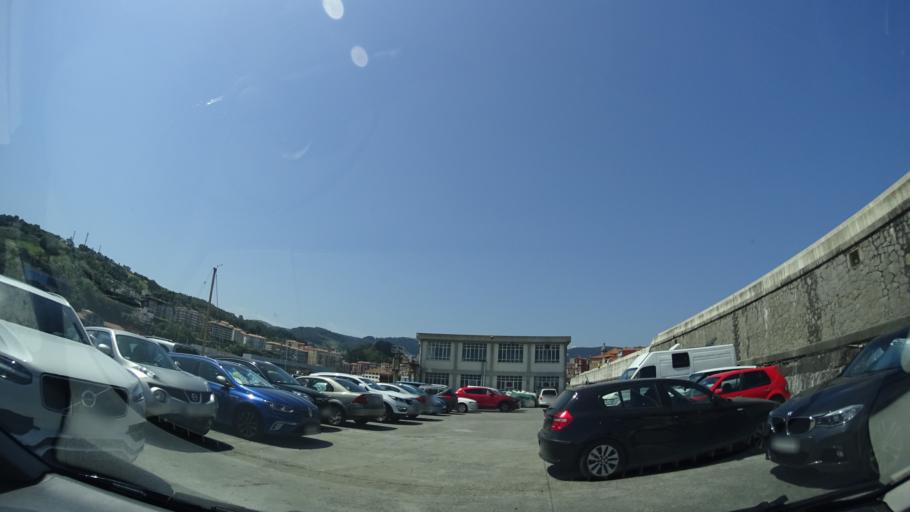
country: ES
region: Basque Country
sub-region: Bizkaia
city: Bermeo
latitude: 43.4204
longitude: -2.7154
